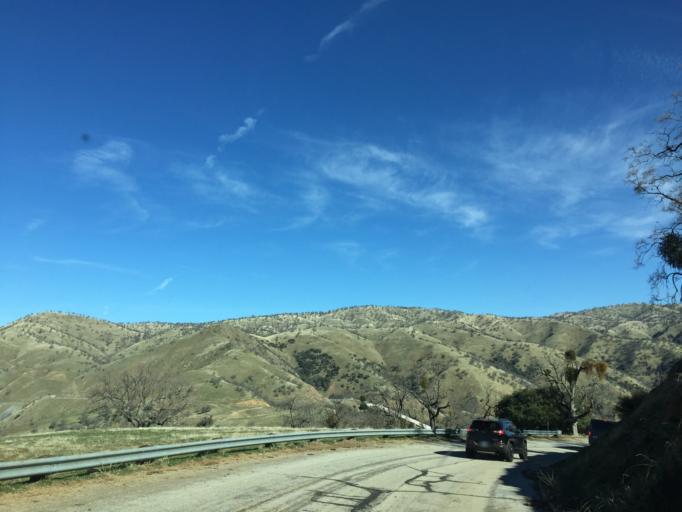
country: US
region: California
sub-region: Kern County
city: Lebec
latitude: 34.8948
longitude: -118.7856
